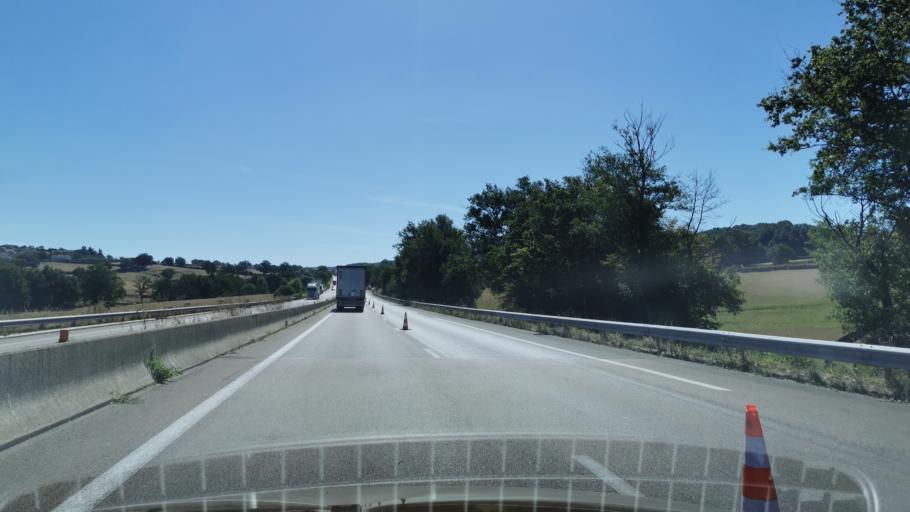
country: FR
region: Bourgogne
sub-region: Departement de Saone-et-Loire
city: Saint-Leu
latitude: 46.7478
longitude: 4.5126
